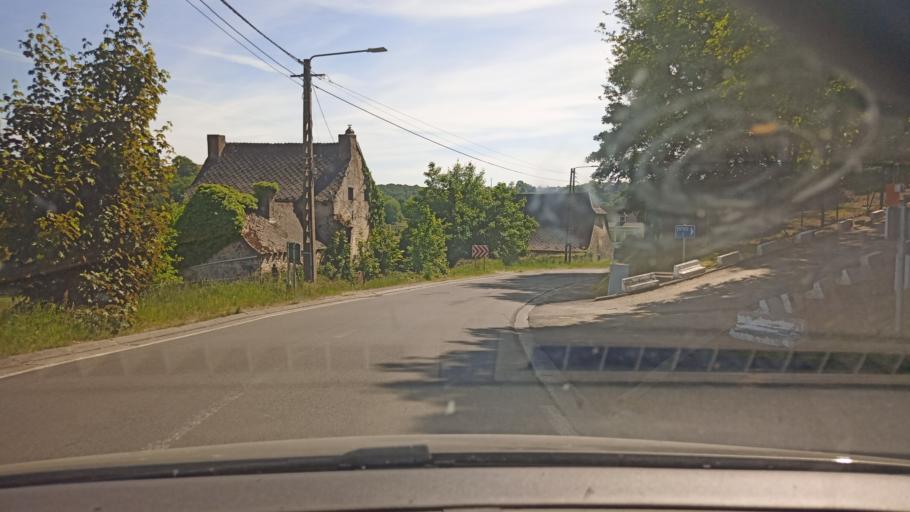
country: BE
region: Wallonia
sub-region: Province du Hainaut
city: Thuin
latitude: 50.3434
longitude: 4.2766
